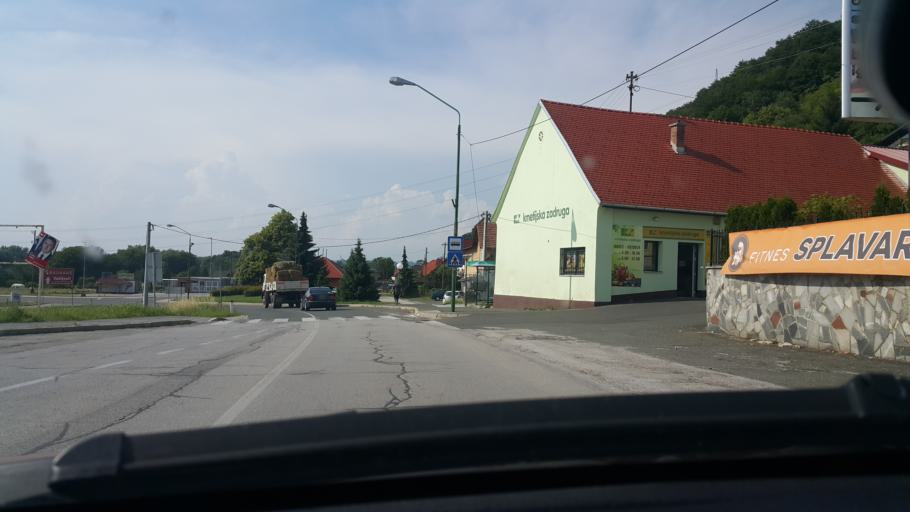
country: SI
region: Duplek
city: Zgornji Duplek
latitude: 46.5142
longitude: 15.7184
